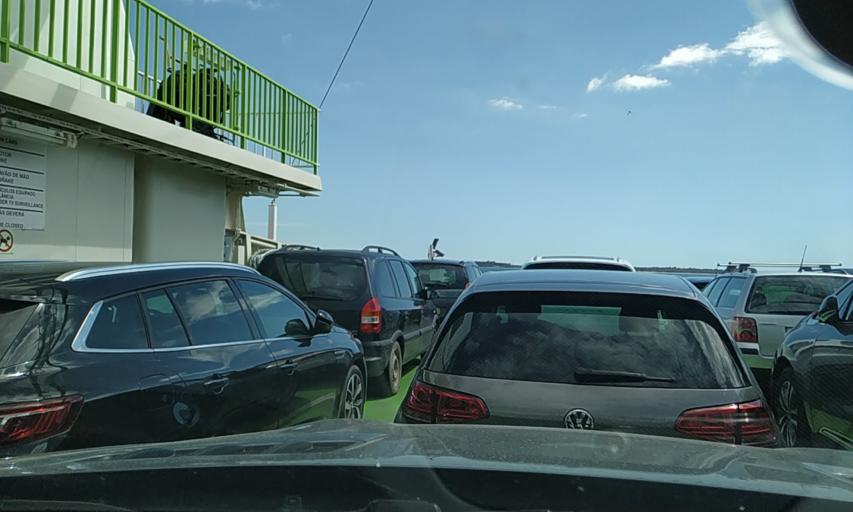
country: PT
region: Setubal
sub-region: Setubal
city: Setubal
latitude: 38.5111
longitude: -8.8854
